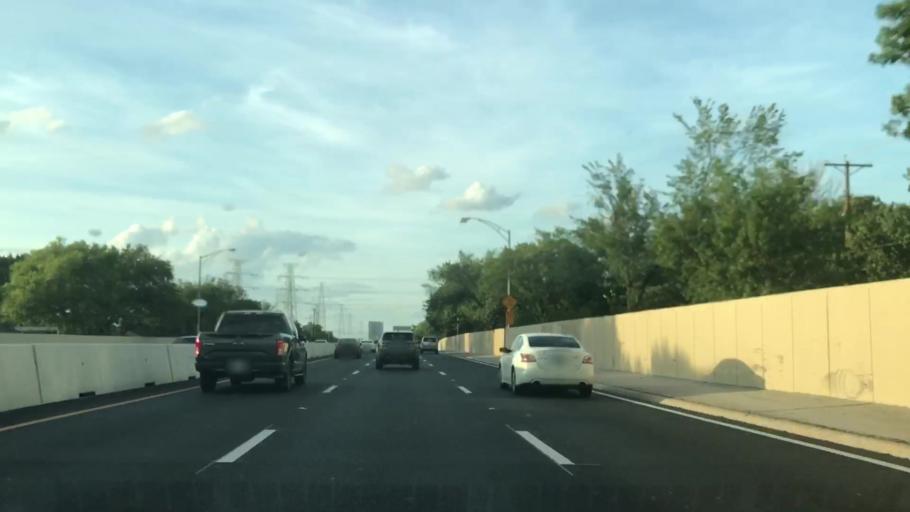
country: US
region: Texas
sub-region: Dallas County
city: University Park
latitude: 32.8989
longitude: -96.8107
